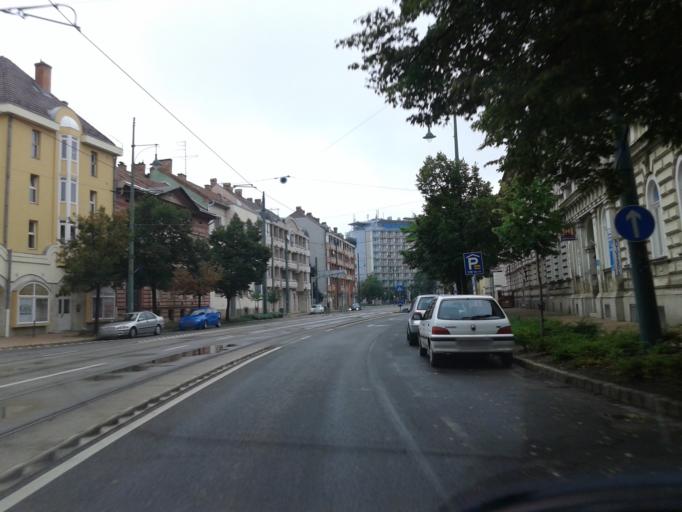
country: HU
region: Csongrad
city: Szeged
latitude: 46.2566
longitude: 20.1534
